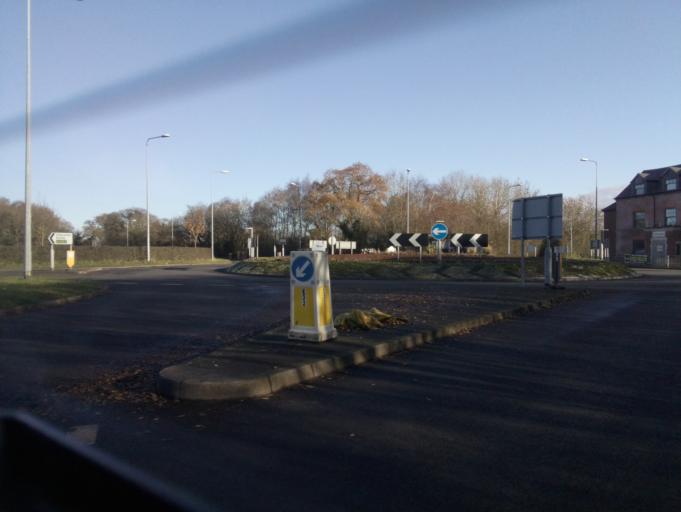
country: GB
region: England
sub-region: Staffordshire
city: Barton under Needwood
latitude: 52.8155
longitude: -1.7361
